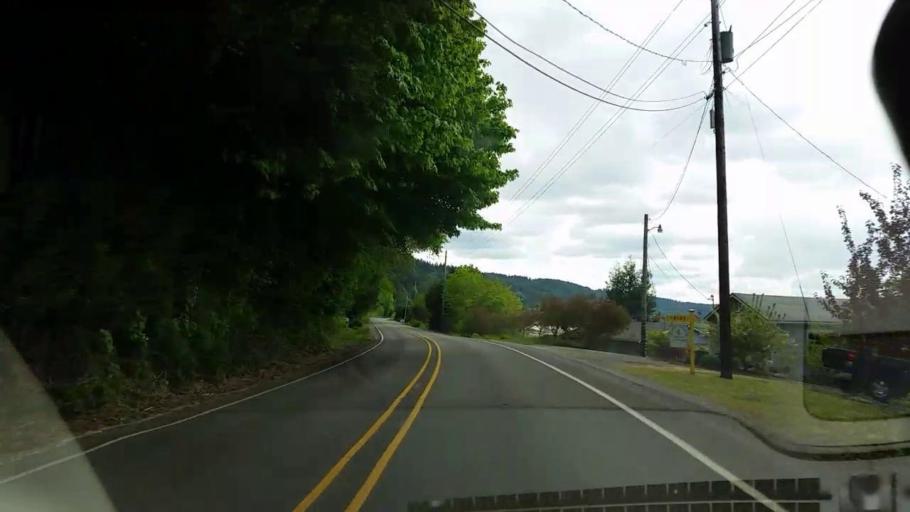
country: US
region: Washington
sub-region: Mason County
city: Shelton
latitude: 47.3473
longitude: -123.1084
